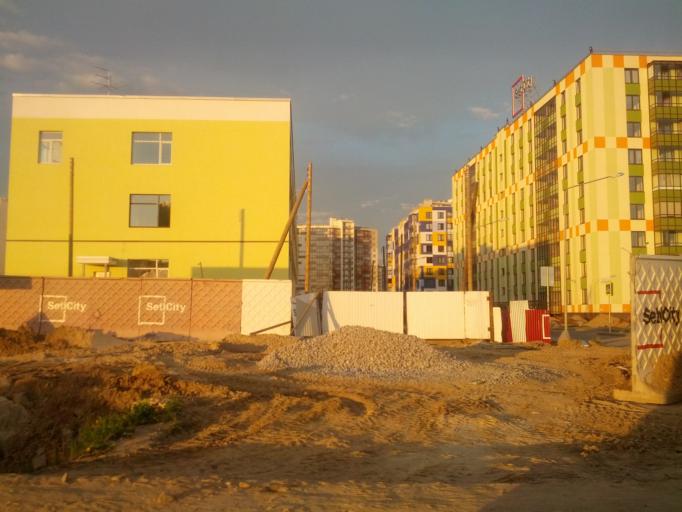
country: RU
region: Leningrad
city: Rybatskoye
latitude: 59.8989
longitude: 30.5049
